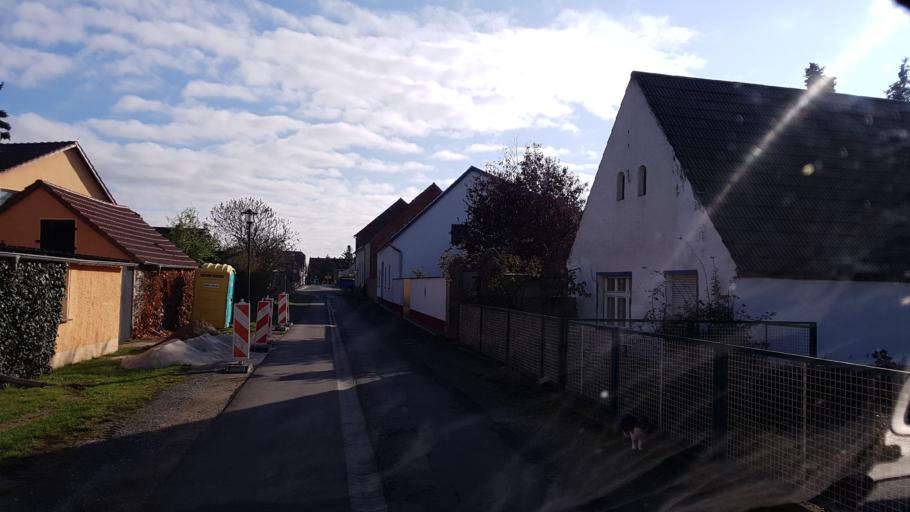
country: DE
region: Brandenburg
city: Doberlug-Kirchhain
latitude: 51.6915
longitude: 13.5103
